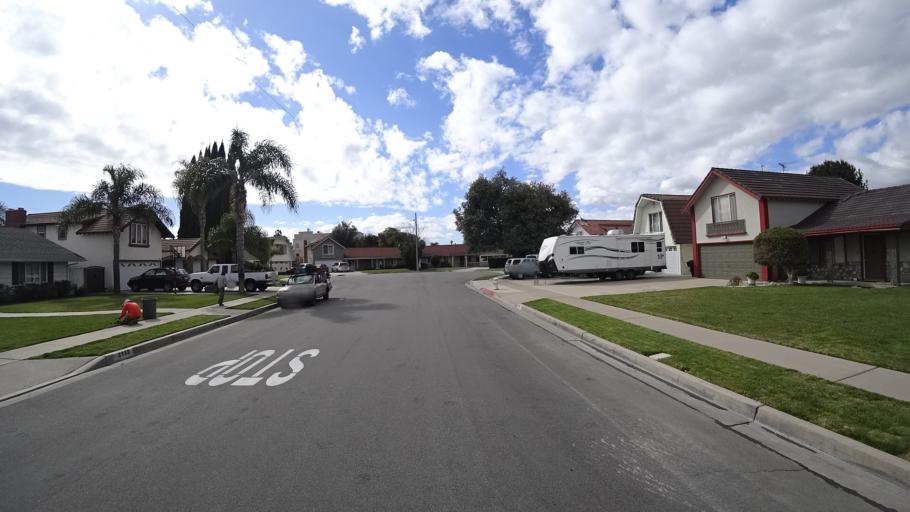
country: US
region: California
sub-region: Orange County
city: Stanton
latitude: 33.8218
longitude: -117.9569
